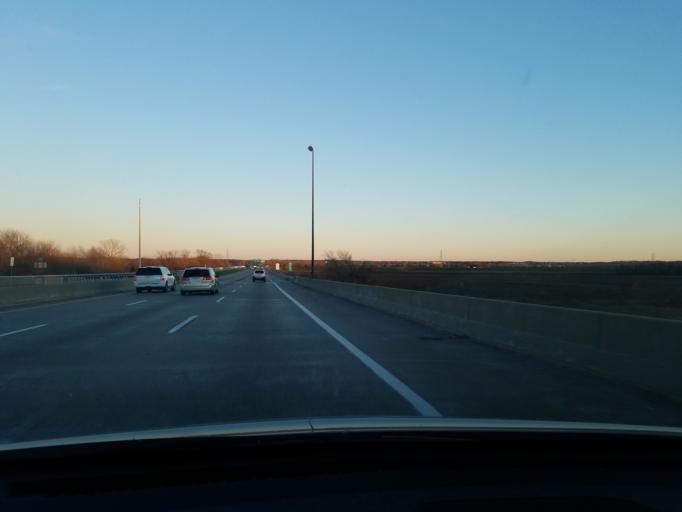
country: US
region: Missouri
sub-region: Saint Louis County
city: Oakville
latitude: 38.4842
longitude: -90.2678
